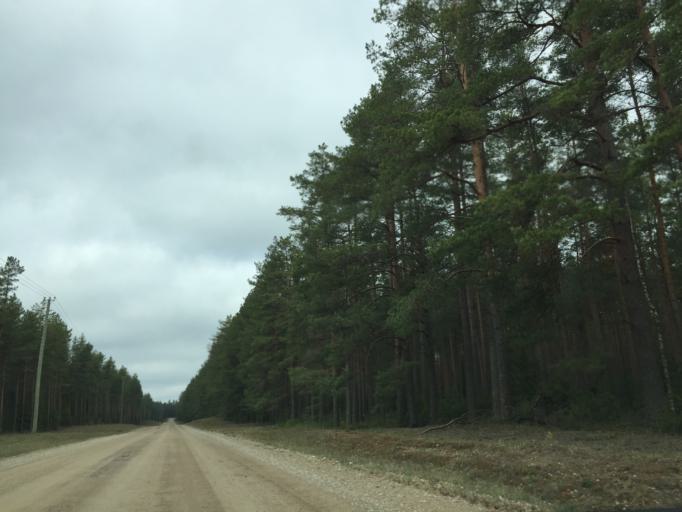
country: EE
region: Valgamaa
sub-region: Valga linn
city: Valga
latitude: 57.6557
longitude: 26.2107
